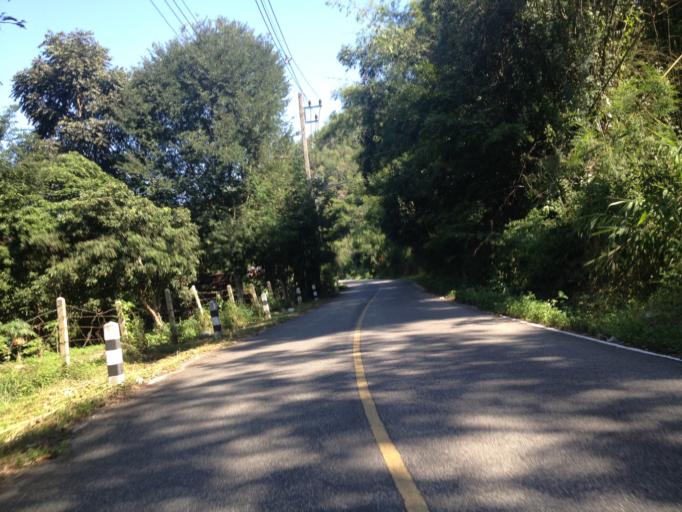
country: TH
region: Chiang Mai
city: Hang Dong
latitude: 18.7578
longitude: 98.9090
